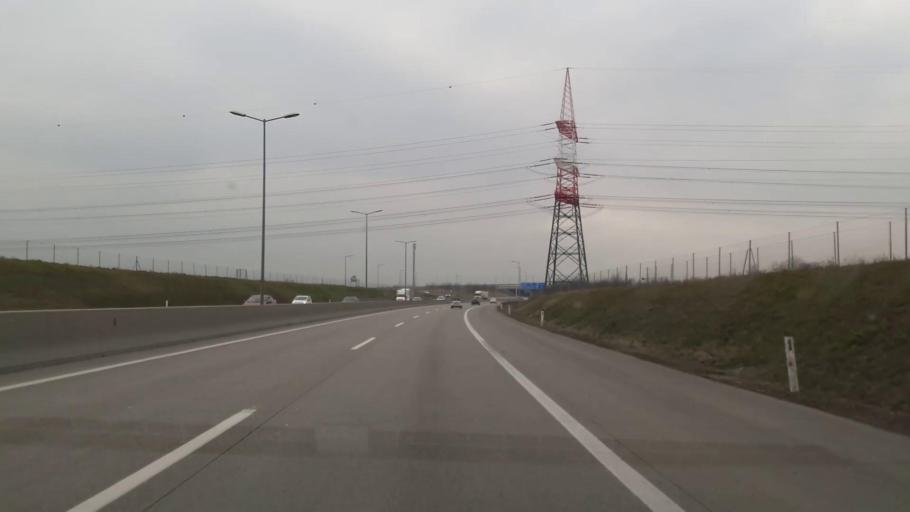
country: AT
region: Lower Austria
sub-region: Politischer Bezirk Wien-Umgebung
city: Leopoldsdorf
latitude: 48.1189
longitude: 16.4182
